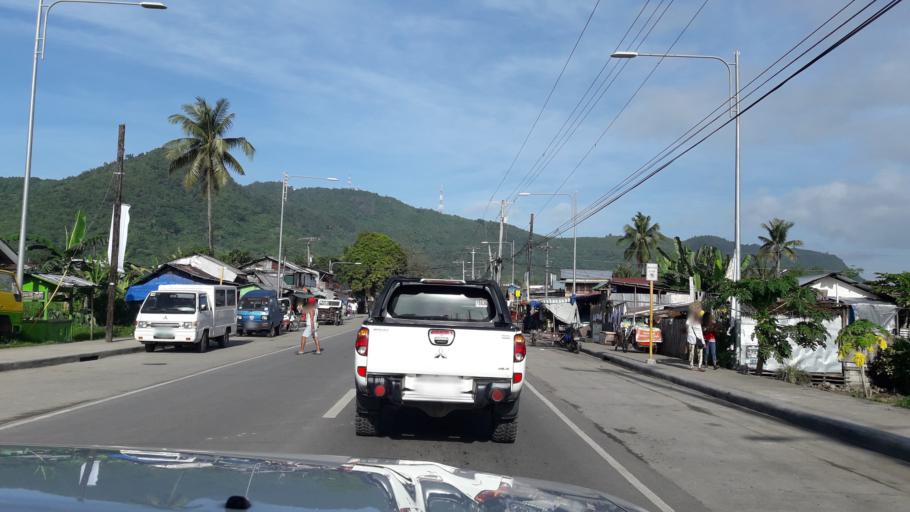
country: PH
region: Eastern Visayas
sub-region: Province of Leyte
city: Panalanoy
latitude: 11.2160
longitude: 124.9970
